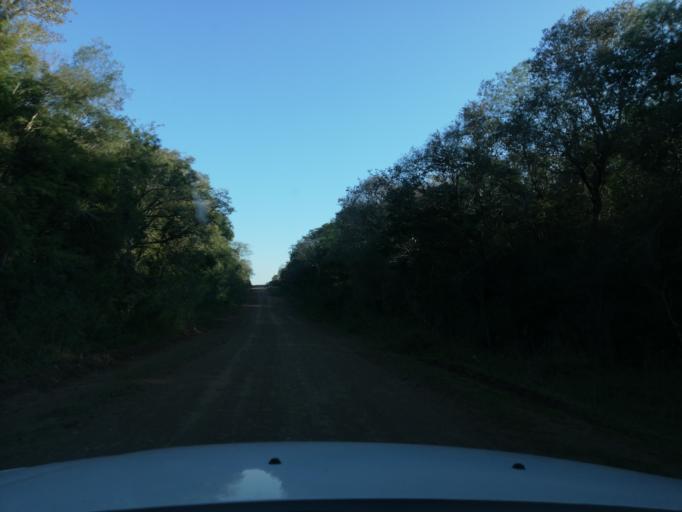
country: AR
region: Misiones
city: Cerro Cora
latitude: -27.5805
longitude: -55.6864
